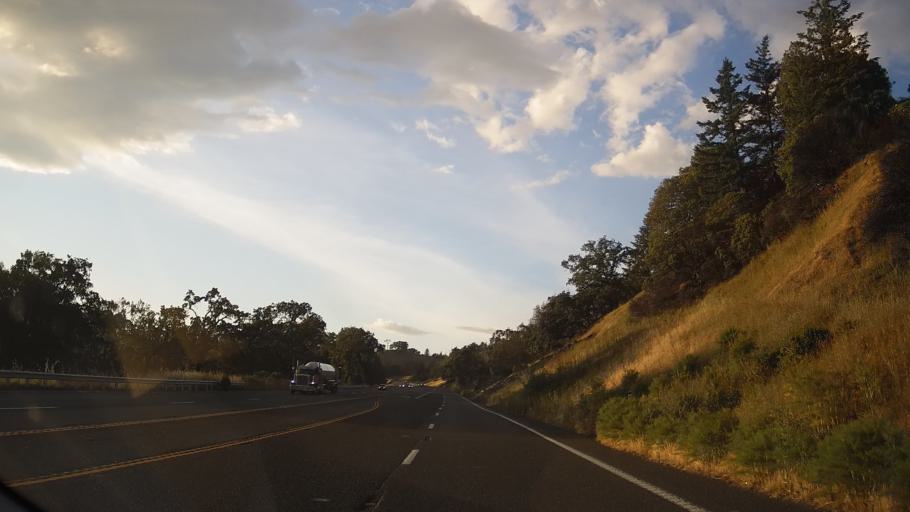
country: US
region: California
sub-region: Mendocino County
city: Willits
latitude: 39.3218
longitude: -123.3008
